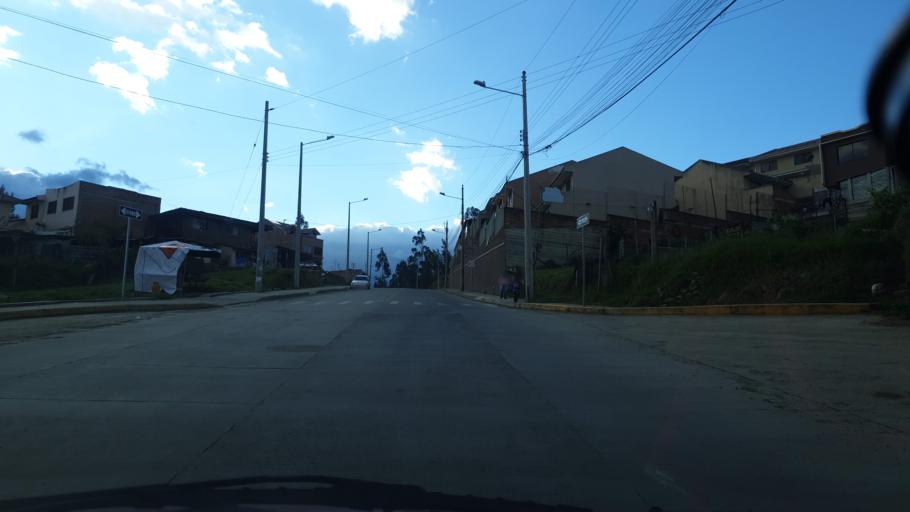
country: EC
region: Azuay
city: Cuenca
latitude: -2.8836
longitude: -79.0452
